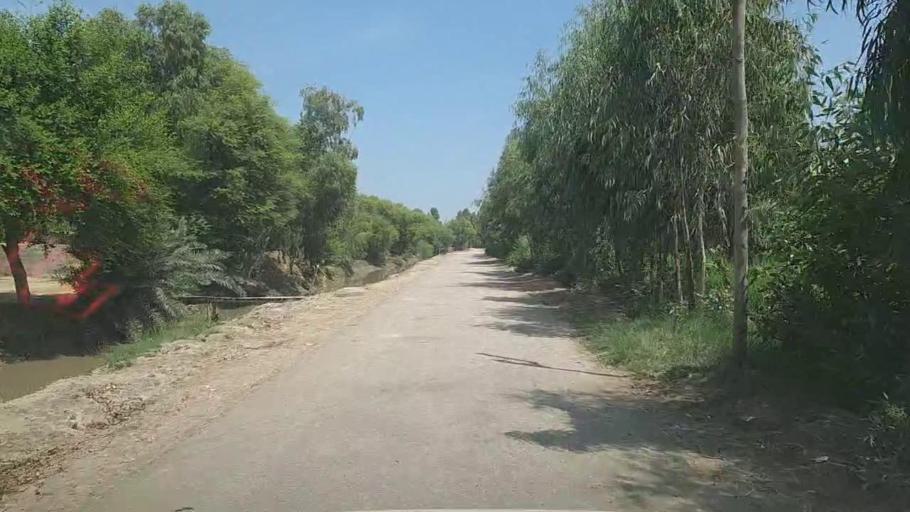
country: PK
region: Sindh
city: Kandhkot
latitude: 28.2675
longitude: 69.2105
